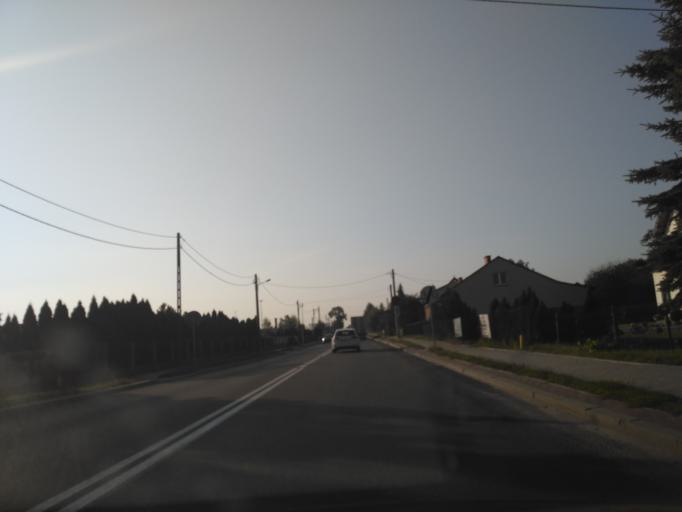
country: PL
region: Lublin Voivodeship
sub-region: Powiat janowski
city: Modliborzyce
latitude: 50.7516
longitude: 22.3339
